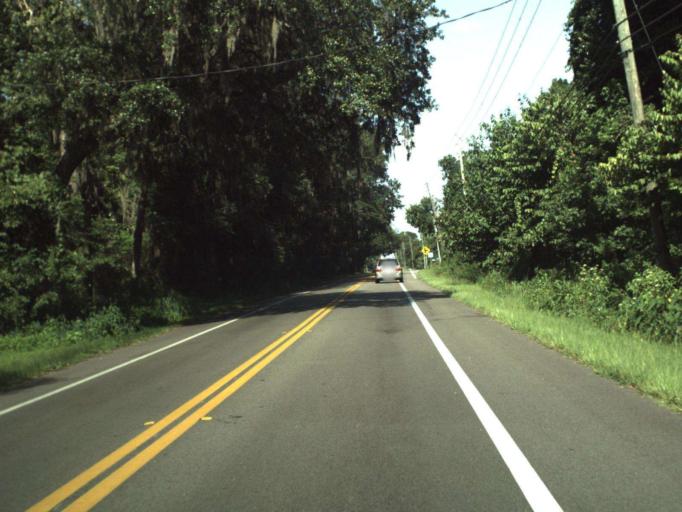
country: US
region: Florida
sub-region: Seminole County
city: Oviedo
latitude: 28.6902
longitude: -81.2214
